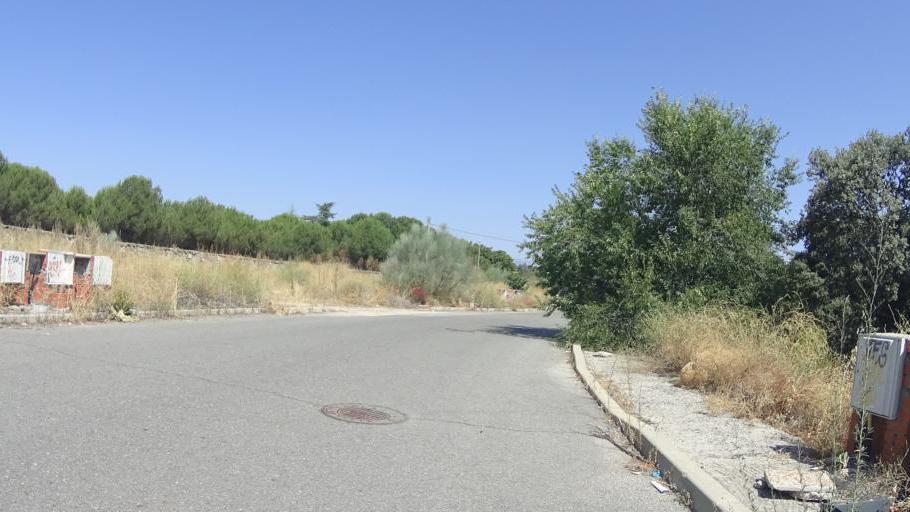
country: ES
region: Madrid
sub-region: Provincia de Madrid
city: Colmenarejo
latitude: 40.5579
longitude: -4.0065
